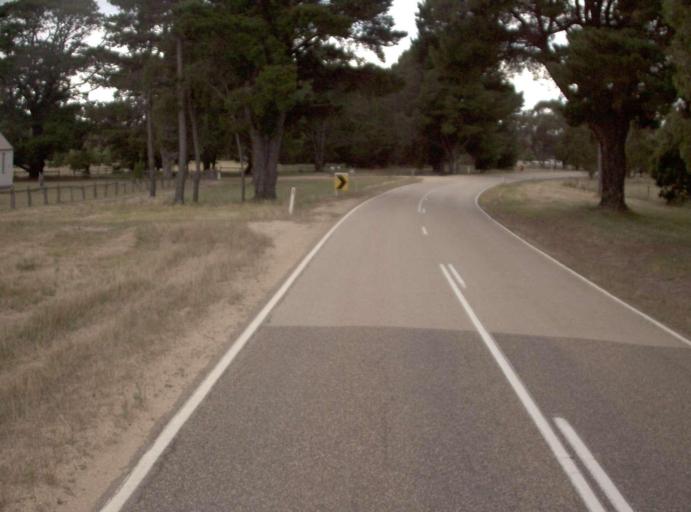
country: AU
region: Victoria
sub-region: Wellington
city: Sale
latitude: -38.0030
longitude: 147.2582
